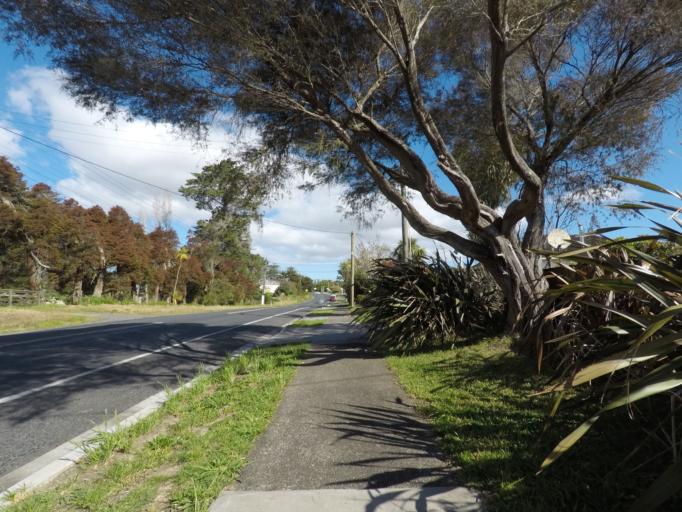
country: NZ
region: Auckland
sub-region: Auckland
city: Rosebank
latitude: -36.8562
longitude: 174.6038
